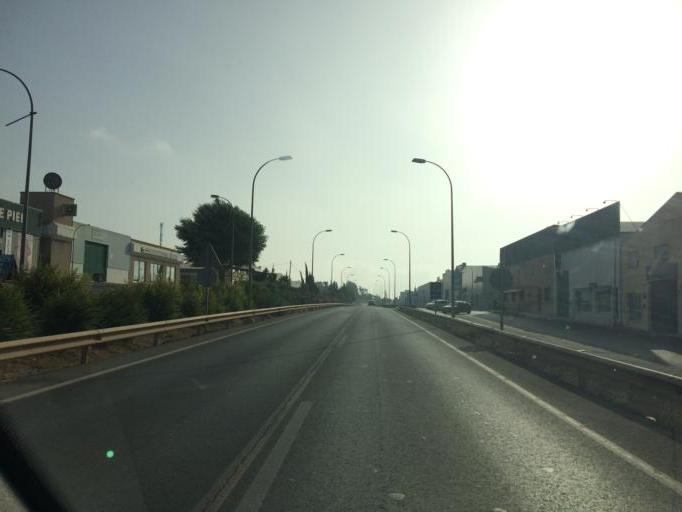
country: ES
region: Andalusia
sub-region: Provincia de Malaga
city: Campillos
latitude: 37.0495
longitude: -4.8750
